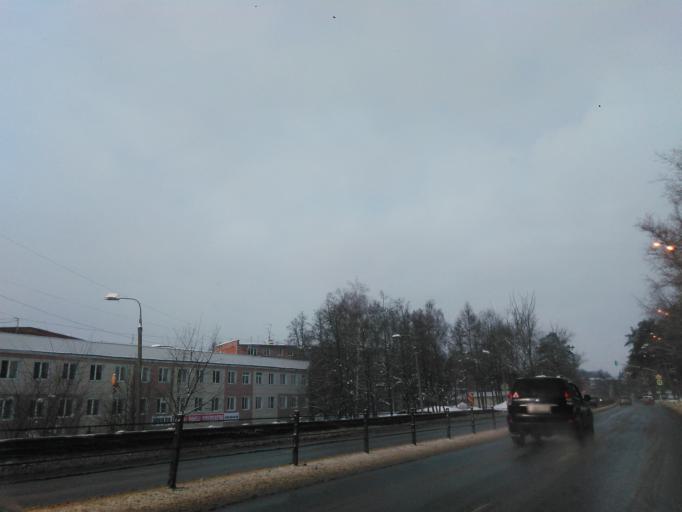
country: RU
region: Moskovskaya
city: Dedenevo
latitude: 56.2349
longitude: 37.5257
